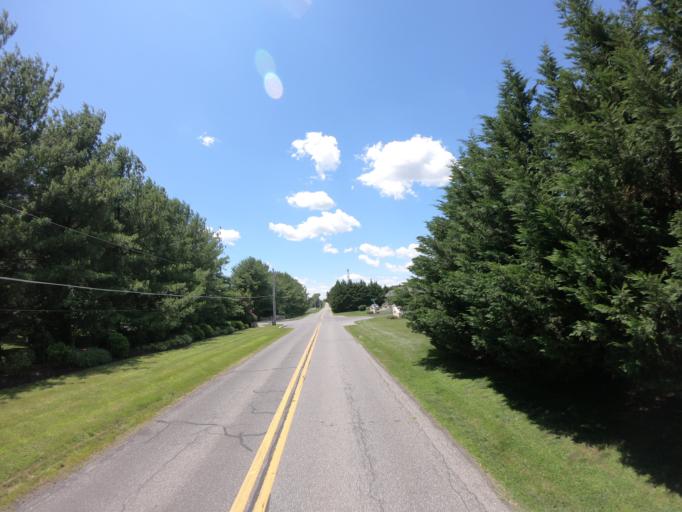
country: US
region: Delaware
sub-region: New Castle County
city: Middletown
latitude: 39.4810
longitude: -75.7688
